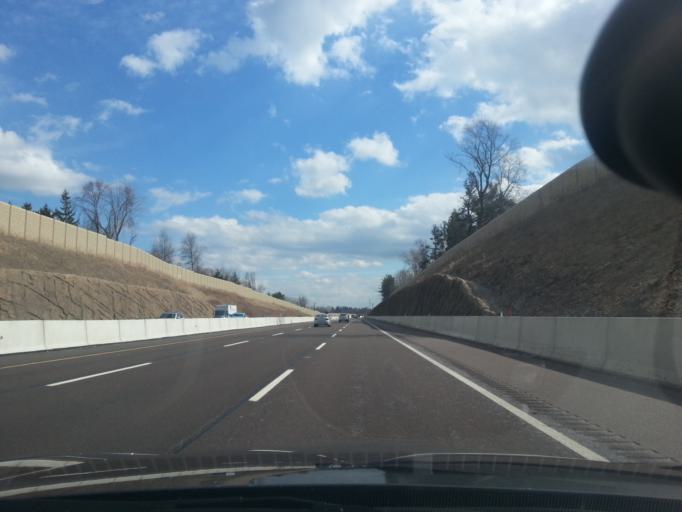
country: US
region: Pennsylvania
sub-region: Montgomery County
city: Blue Bell
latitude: 40.1589
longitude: -75.2979
